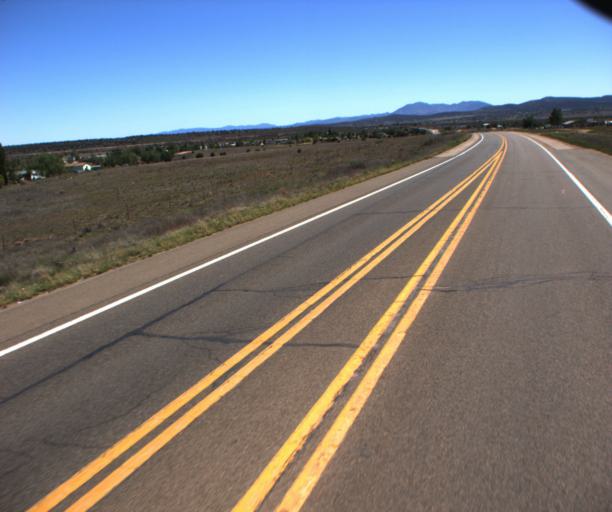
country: US
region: Arizona
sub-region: Yavapai County
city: Paulden
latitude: 34.9087
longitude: -112.4615
